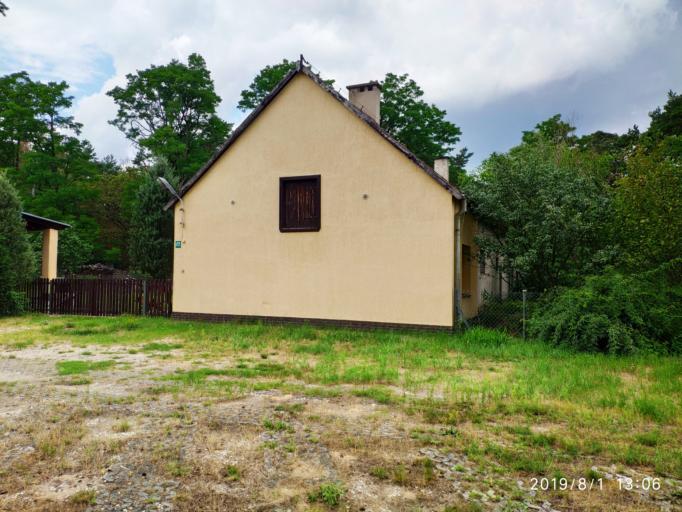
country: PL
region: Lubusz
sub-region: Powiat zielonogorski
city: Nowogrod Bobrzanski
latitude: 51.8155
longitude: 15.2805
